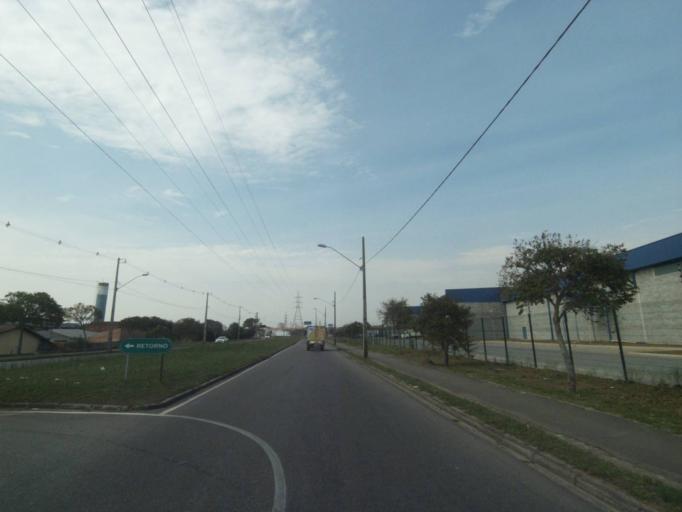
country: BR
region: Parana
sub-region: Sao Jose Dos Pinhais
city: Sao Jose dos Pinhais
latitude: -25.5043
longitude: -49.2122
